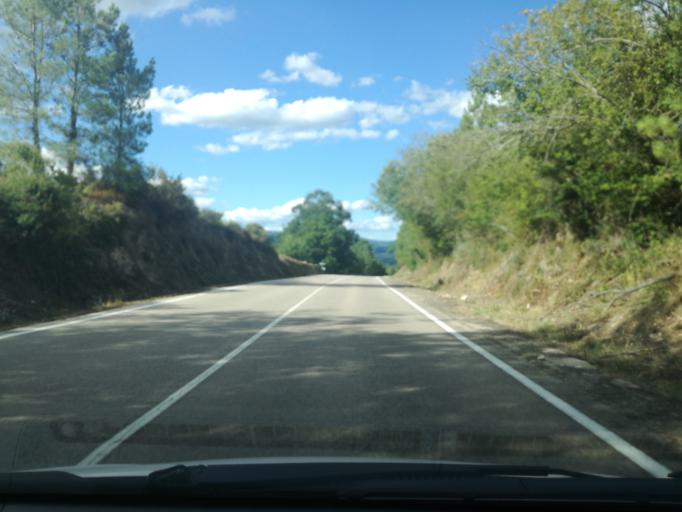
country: ES
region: Galicia
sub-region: Provincia de Ourense
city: Lobios
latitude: 41.8911
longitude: -8.0889
